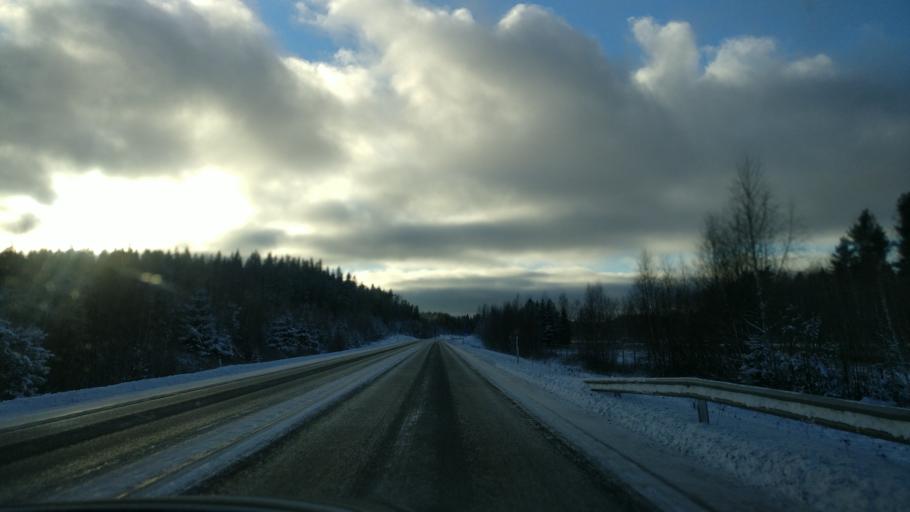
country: FI
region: Southern Savonia
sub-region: Mikkeli
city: Pertunmaa
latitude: 61.4249
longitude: 26.4517
